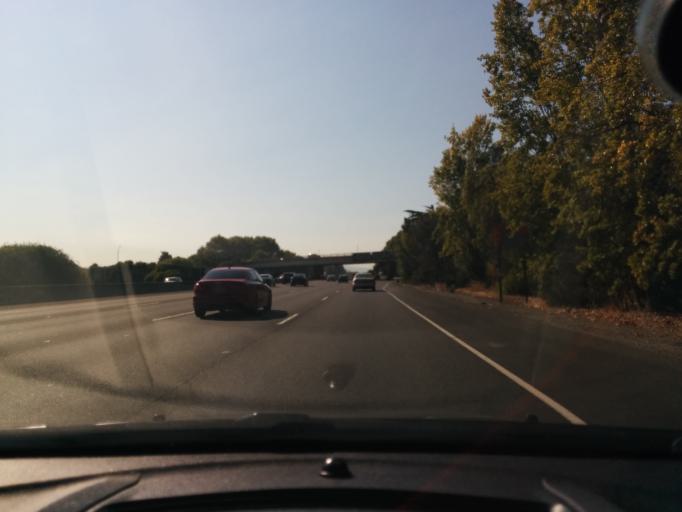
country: US
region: California
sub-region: Santa Clara County
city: Sunnyvale
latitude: 37.4004
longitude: -122.0334
